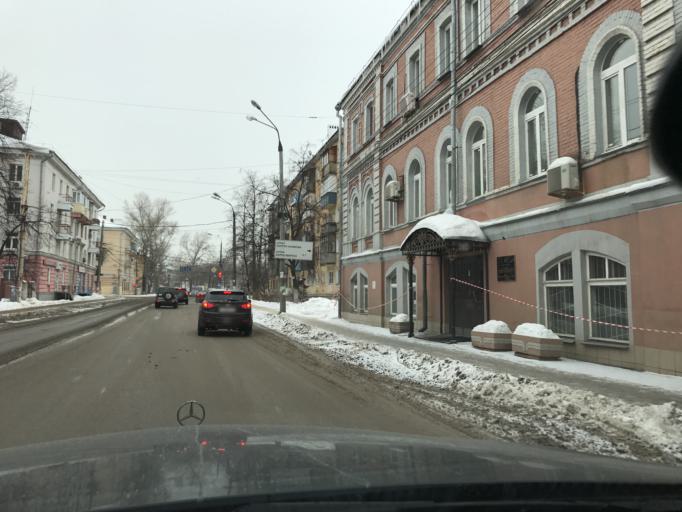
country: RU
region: Nizjnij Novgorod
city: Nizhniy Novgorod
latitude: 56.3274
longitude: 43.9548
